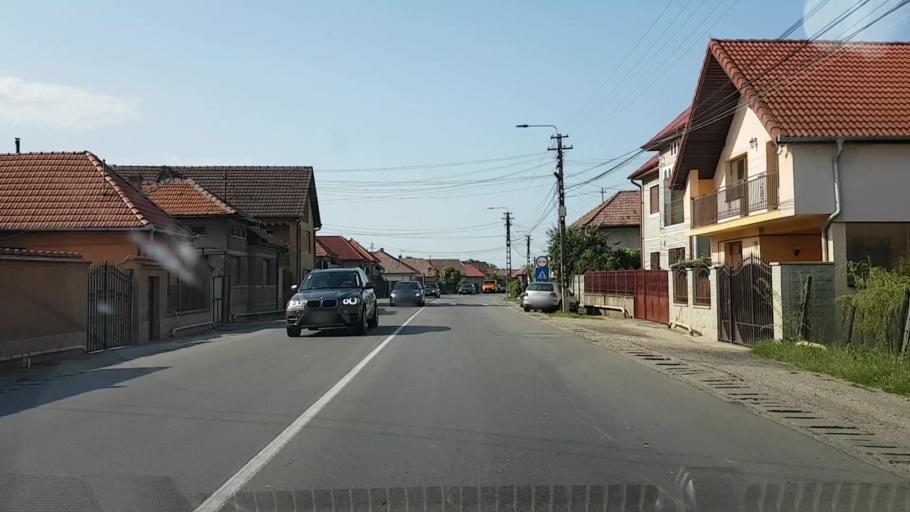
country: RO
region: Alba
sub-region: Municipiul Sebes
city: Lancram
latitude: 45.9855
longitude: 23.5553
